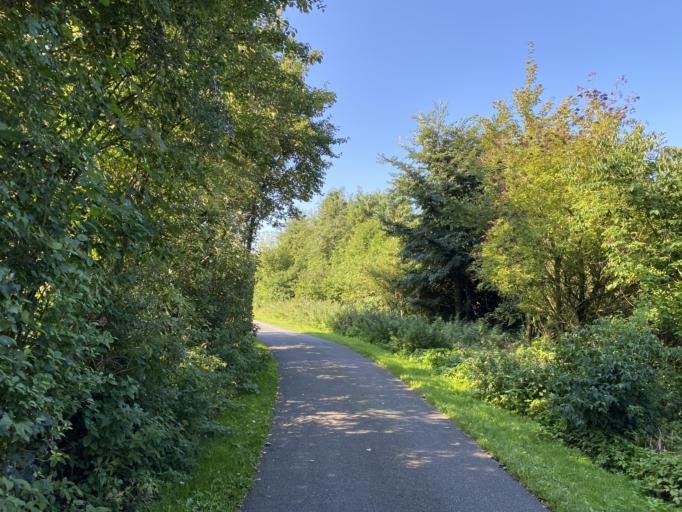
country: DK
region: South Denmark
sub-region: Nyborg Kommune
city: Nyborg
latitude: 55.2383
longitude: 10.7041
